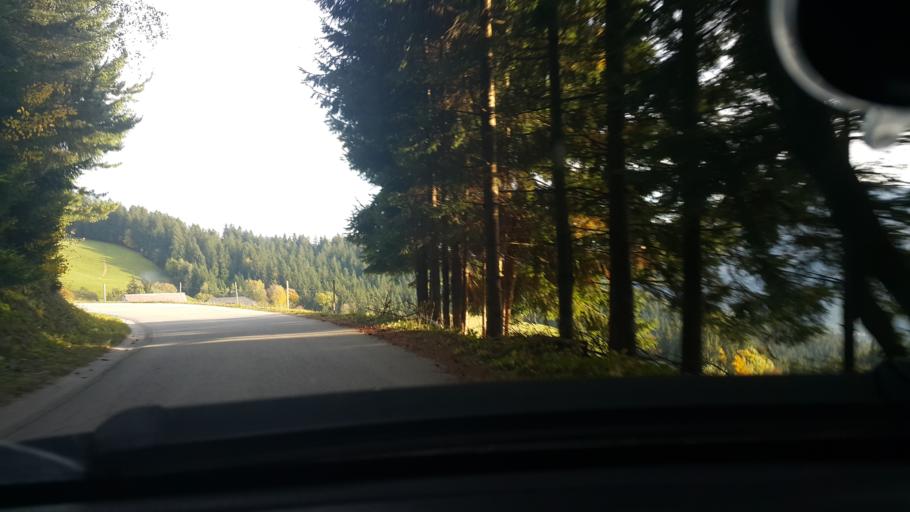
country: SI
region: Mislinja
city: Mislinja
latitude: 46.4273
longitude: 15.2596
